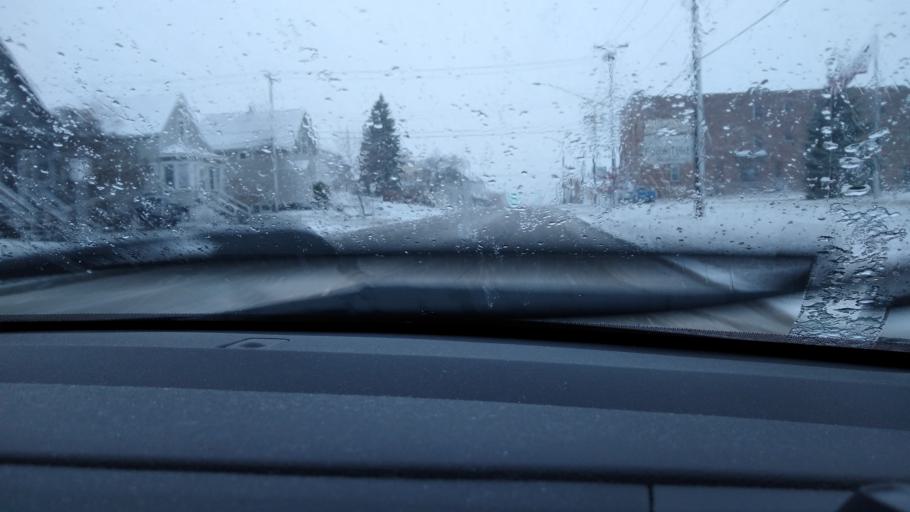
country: US
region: Michigan
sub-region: Delta County
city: Escanaba
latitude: 45.7494
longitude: -87.0687
